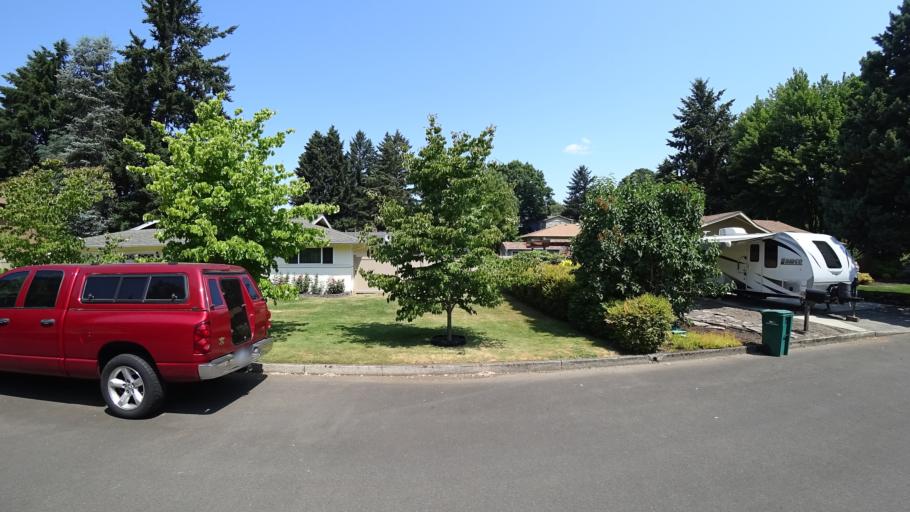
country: US
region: Oregon
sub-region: Clackamas County
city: Oatfield
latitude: 45.4441
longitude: -122.5848
